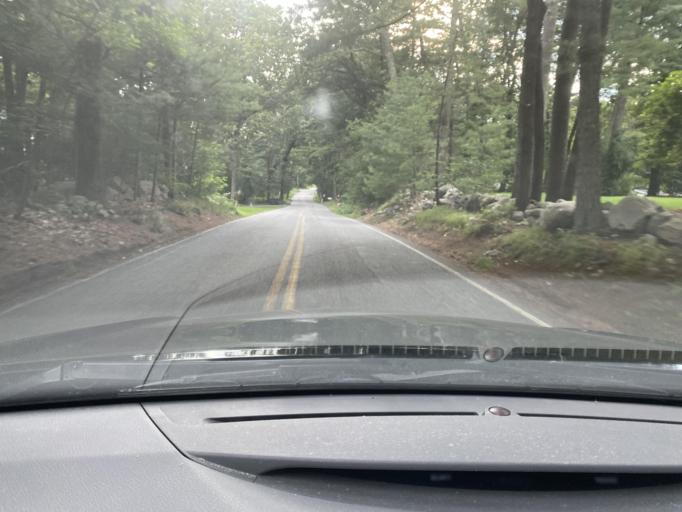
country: US
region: Massachusetts
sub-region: Norfolk County
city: Medfield
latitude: 42.1766
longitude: -71.2697
